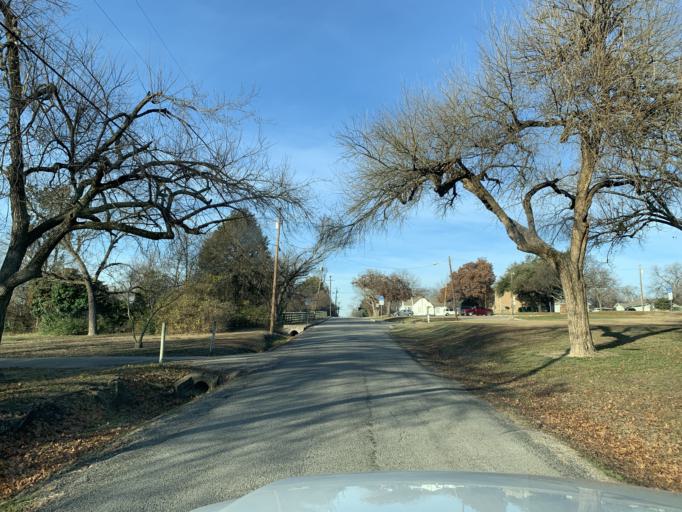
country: US
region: Texas
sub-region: Collin County
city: McKinney
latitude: 33.1900
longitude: -96.6208
